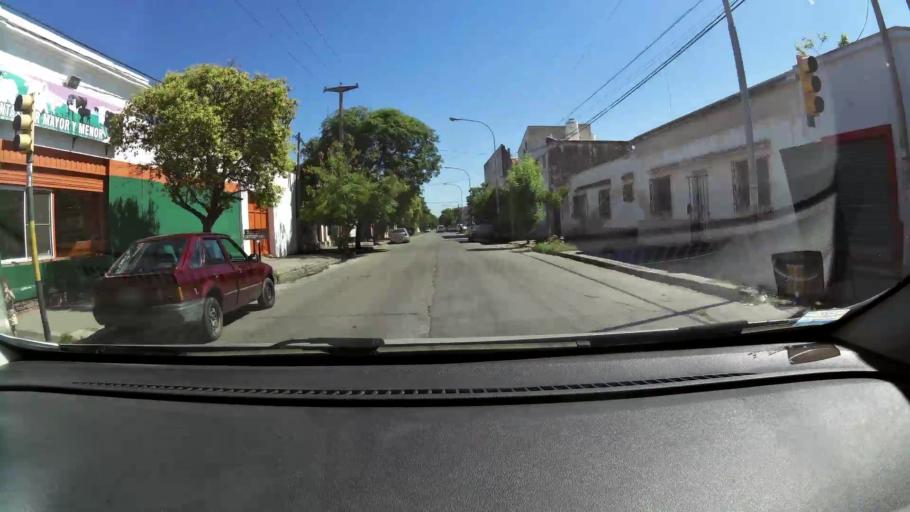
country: AR
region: Cordoba
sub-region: Departamento de Capital
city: Cordoba
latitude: -31.4235
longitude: -64.1582
